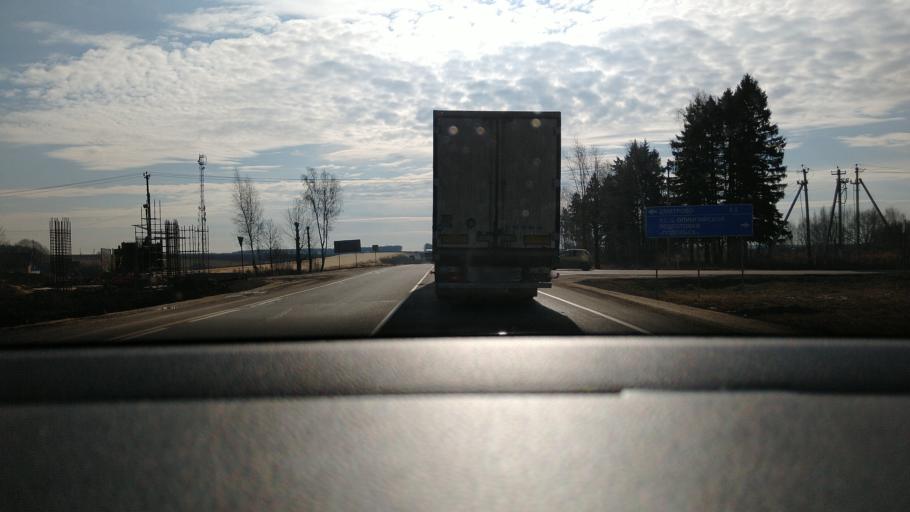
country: RU
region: Moskovskaya
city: Dubrovitsy
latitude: 55.3651
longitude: 37.4273
